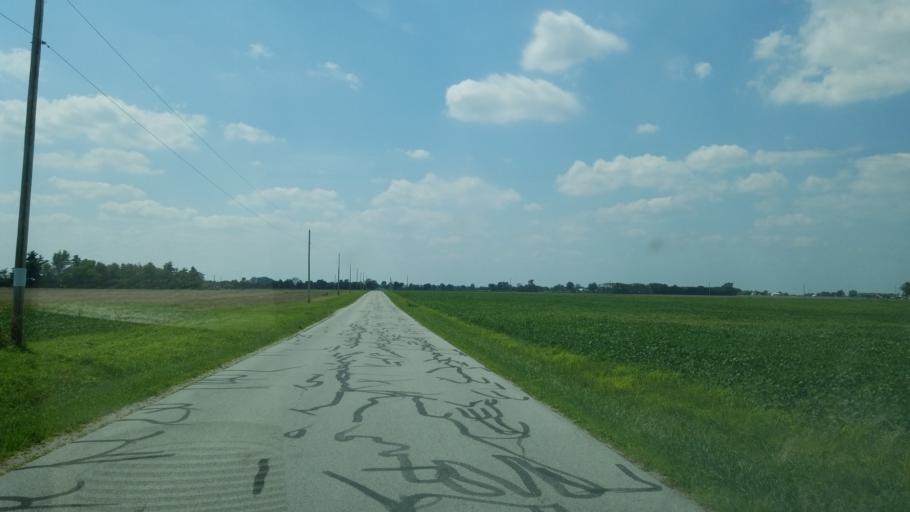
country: US
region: Ohio
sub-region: Seneca County
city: Tiffin
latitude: 41.1527
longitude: -83.2226
